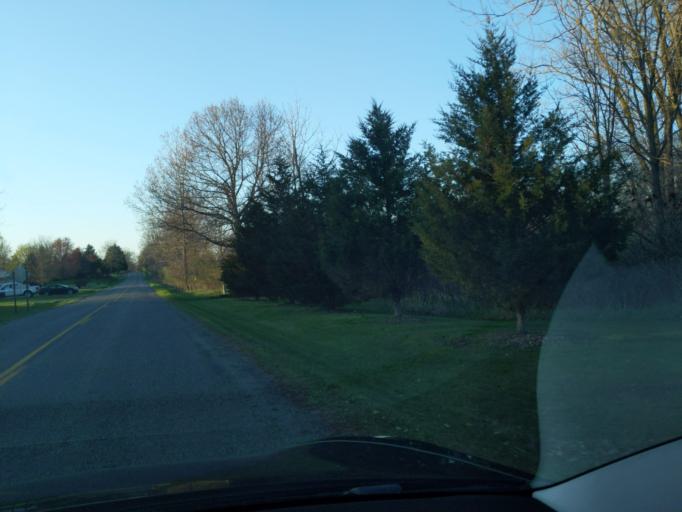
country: US
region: Michigan
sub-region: Ingham County
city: Stockbridge
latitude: 42.4844
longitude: -84.2397
